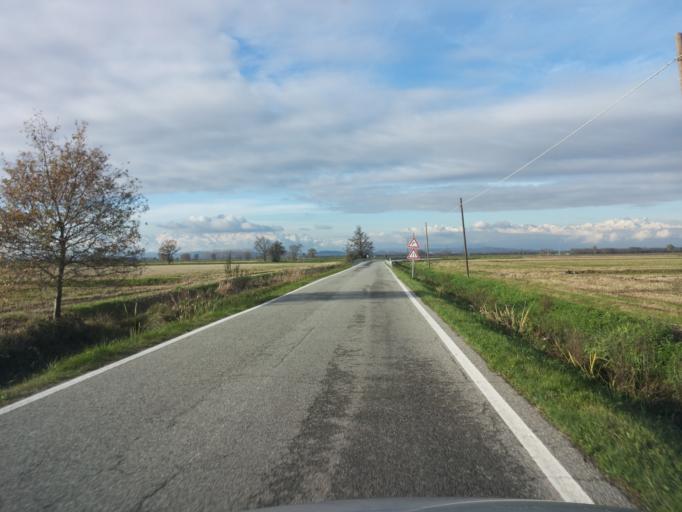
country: IT
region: Piedmont
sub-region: Provincia di Vercelli
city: Crova
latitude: 45.3085
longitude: 8.2039
